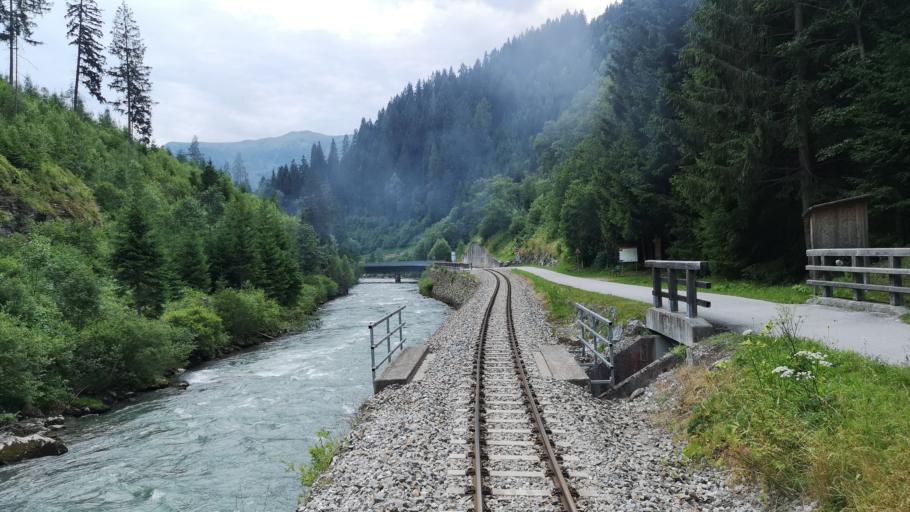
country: AT
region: Salzburg
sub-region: Politischer Bezirk Tamsweg
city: Ramingstein
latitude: 47.0852
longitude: 13.8149
